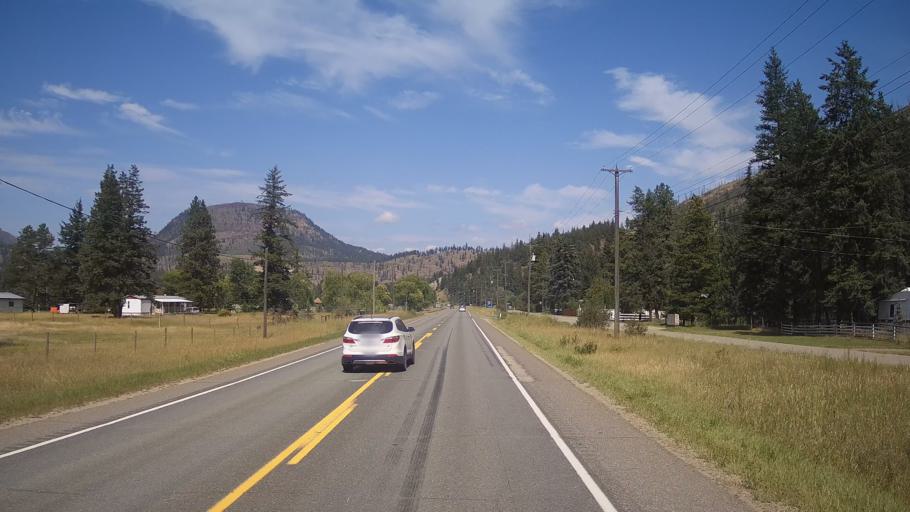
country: CA
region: British Columbia
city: Kamloops
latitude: 51.0640
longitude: -120.2161
